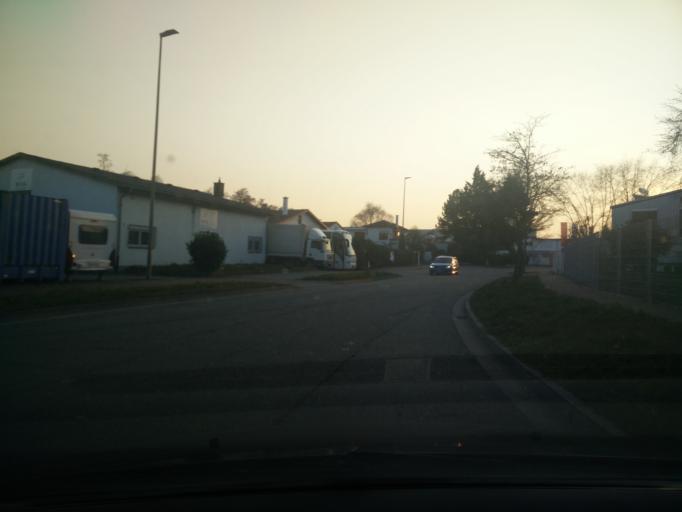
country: DE
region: Rheinland-Pfalz
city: Kandel
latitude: 49.0988
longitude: 8.1804
